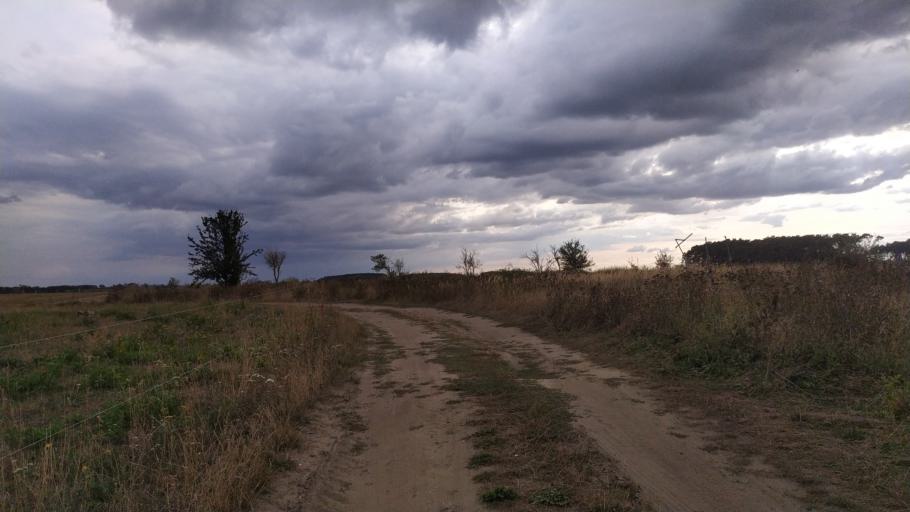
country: DE
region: Mecklenburg-Vorpommern
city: Wolgast
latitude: 54.0565
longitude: 13.8238
